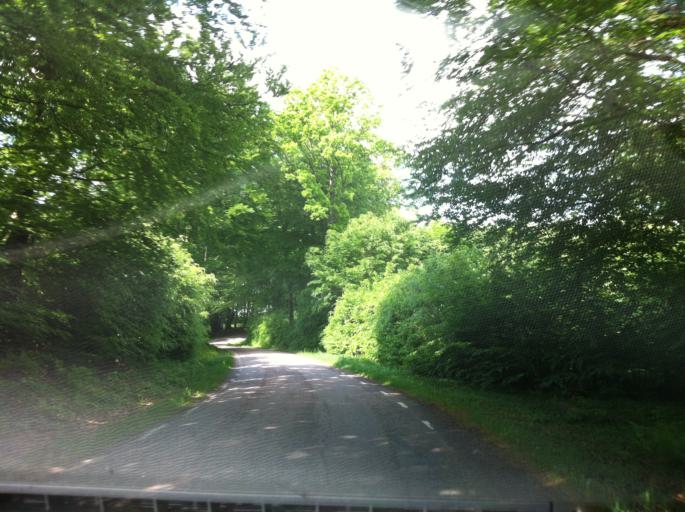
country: SE
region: Skane
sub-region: Svalovs Kommun
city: Kagerod
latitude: 56.0288
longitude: 13.1586
